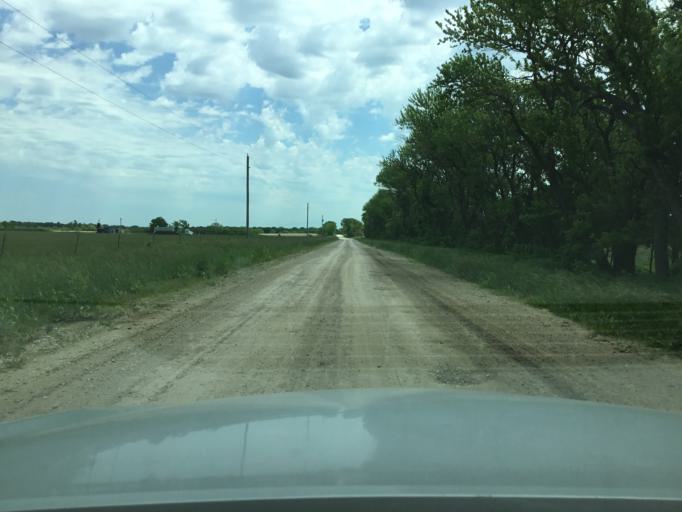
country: US
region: Kansas
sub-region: Montgomery County
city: Caney
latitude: 37.0951
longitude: -95.8049
